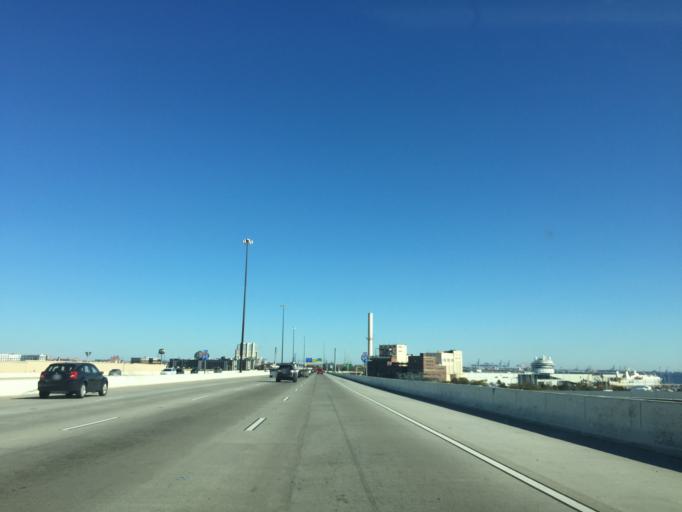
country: US
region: Maryland
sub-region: City of Baltimore
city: Baltimore
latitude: 39.2667
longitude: -76.6112
